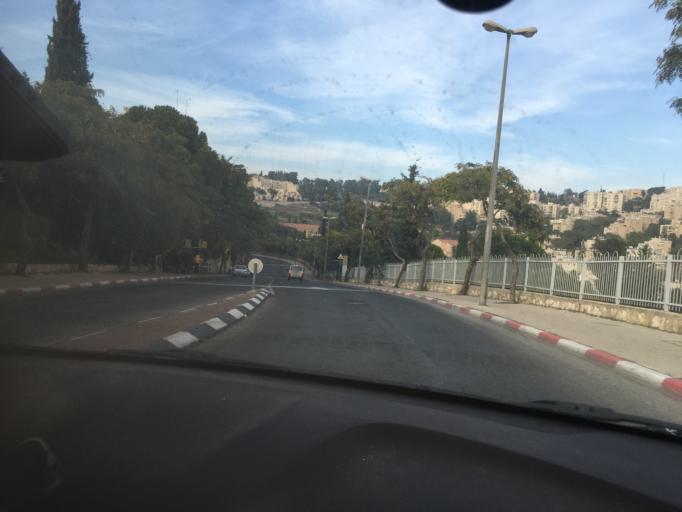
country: PS
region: West Bank
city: Ash Shaykh Sa`d
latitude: 31.7464
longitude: 35.2330
